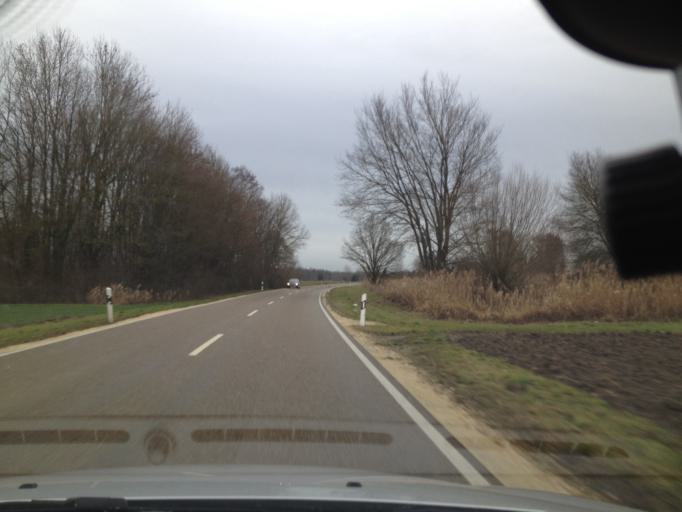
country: DE
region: Bavaria
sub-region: Swabia
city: Gundelfingen
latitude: 48.5227
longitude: 10.3684
